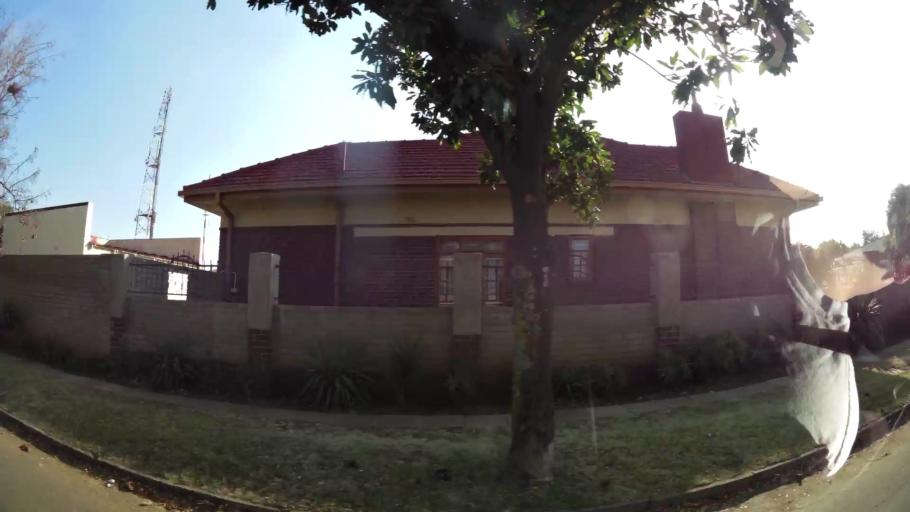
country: ZA
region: Gauteng
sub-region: West Rand District Municipality
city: Randfontein
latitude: -26.1770
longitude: 27.7063
